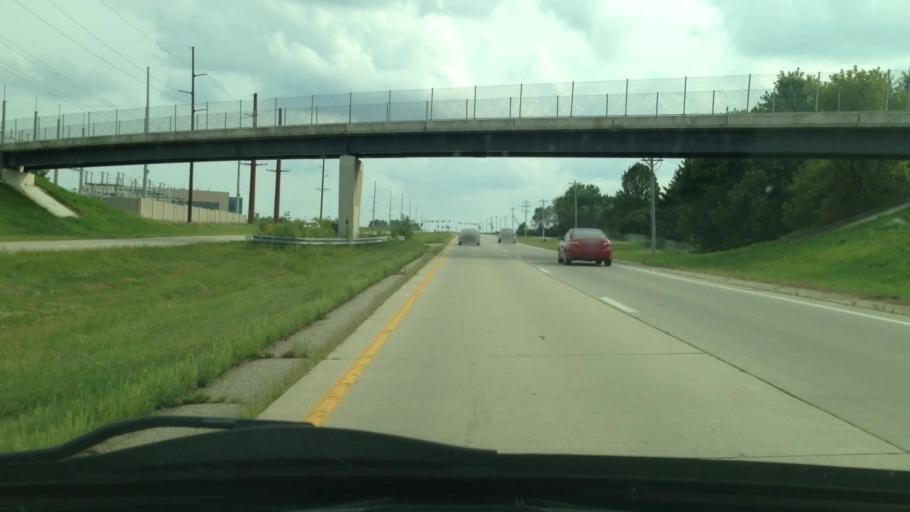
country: US
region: Minnesota
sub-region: Olmsted County
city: Rochester
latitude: 44.0746
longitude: -92.5235
